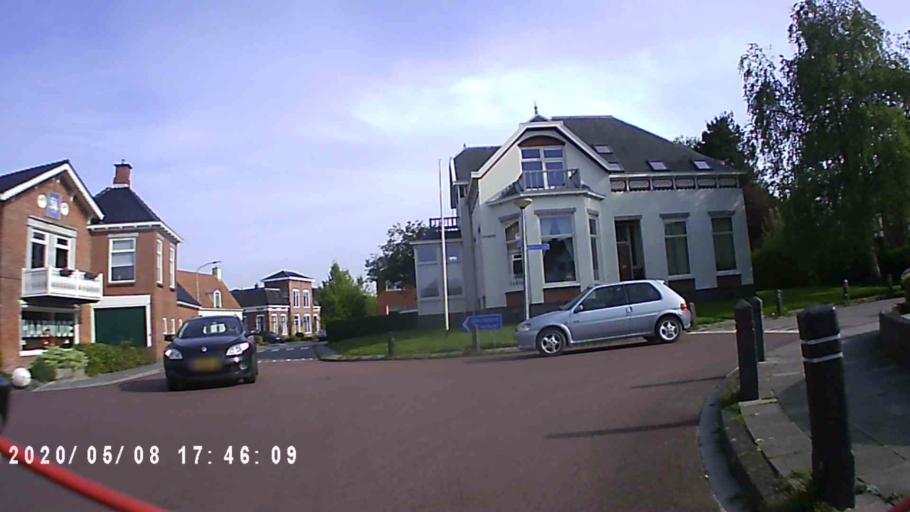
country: NL
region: Groningen
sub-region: Gemeente Winsum
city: Winsum
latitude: 53.3643
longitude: 6.5161
